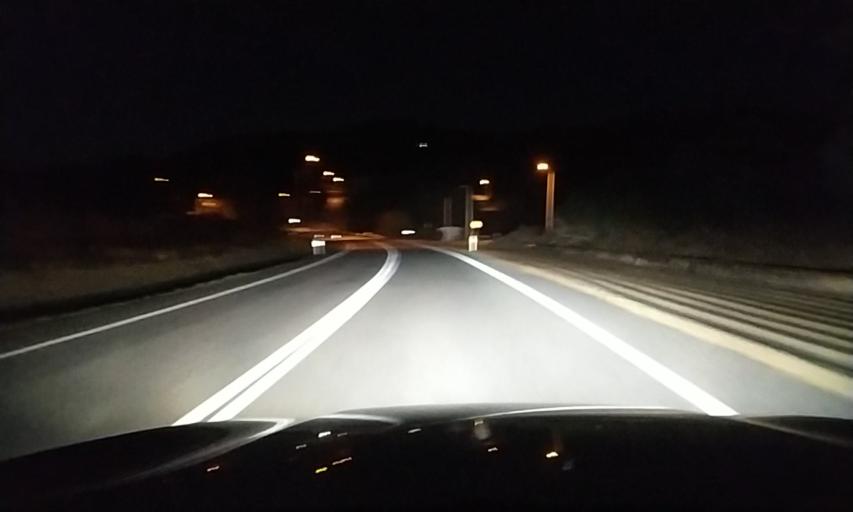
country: ES
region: Galicia
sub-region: Provincia de Ourense
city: Cualedro
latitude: 41.9707
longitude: -7.5202
